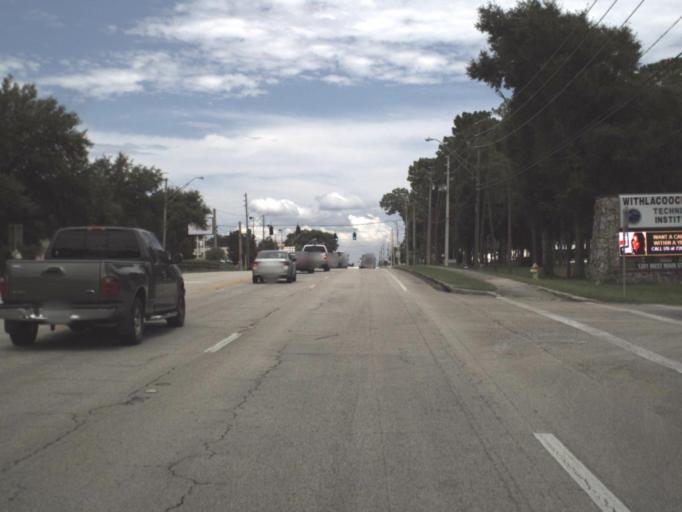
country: US
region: Florida
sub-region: Citrus County
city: Inverness
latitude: 28.8359
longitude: -82.3464
